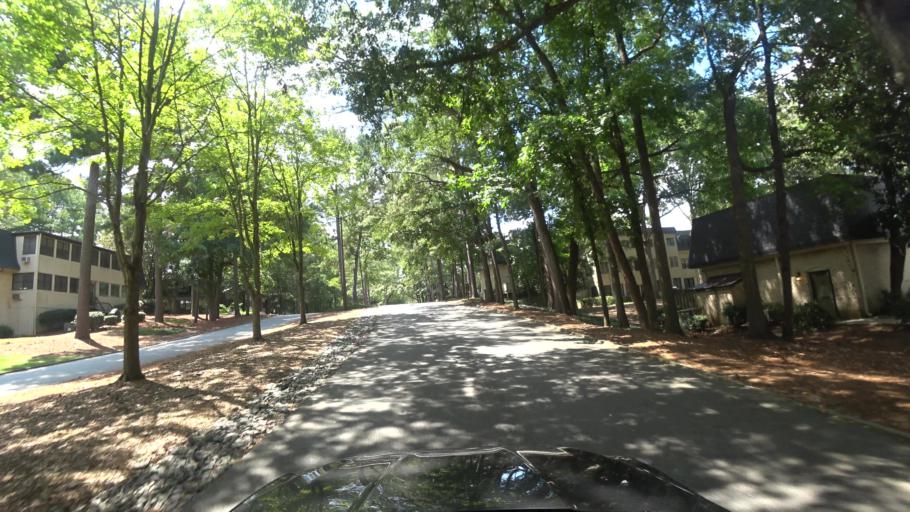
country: US
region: Georgia
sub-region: Cobb County
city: Vinings
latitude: 33.8204
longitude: -84.4255
